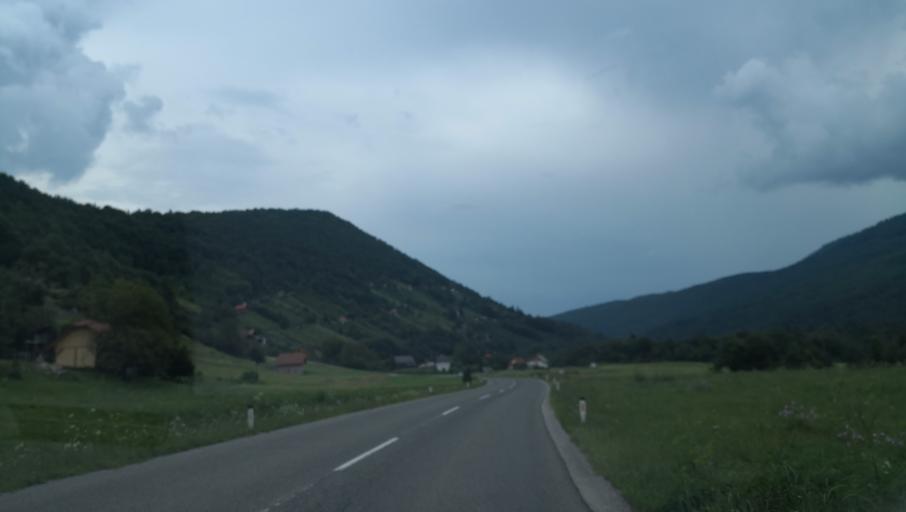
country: SI
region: Zuzemberk
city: Zuzemberk
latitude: 45.7987
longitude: 14.9797
